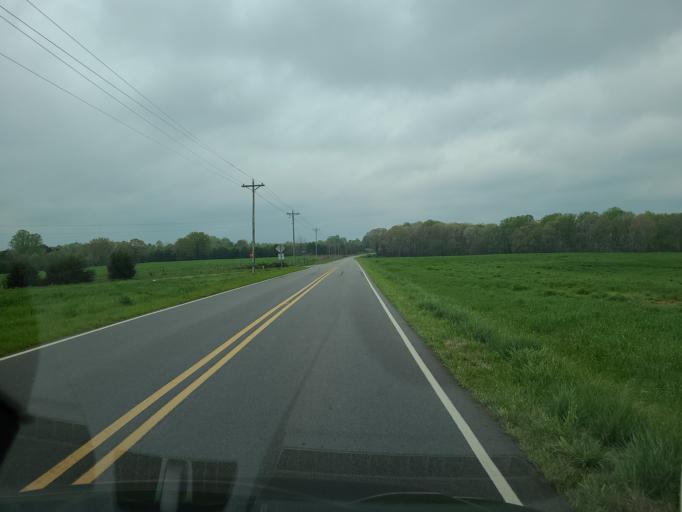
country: US
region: North Carolina
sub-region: Gaston County
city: Cherryville
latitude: 35.4351
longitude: -81.3915
